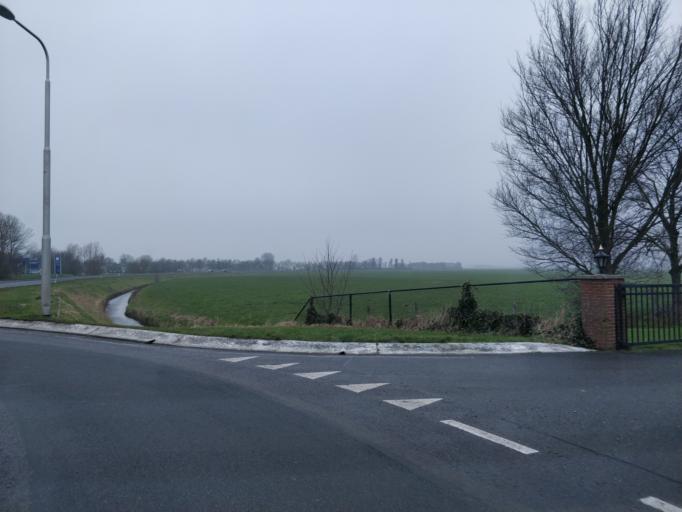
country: NL
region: Friesland
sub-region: Menameradiel
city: Berltsum
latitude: 53.2409
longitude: 5.6680
